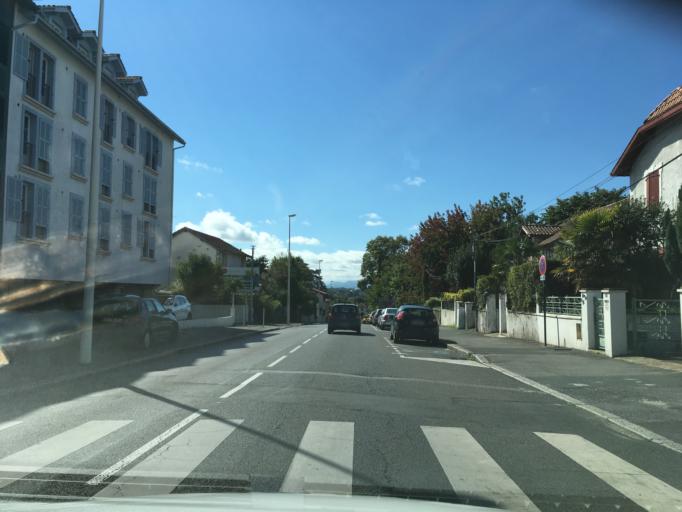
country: FR
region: Aquitaine
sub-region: Departement des Pyrenees-Atlantiques
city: Bayonne
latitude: 43.5027
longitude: -1.4678
